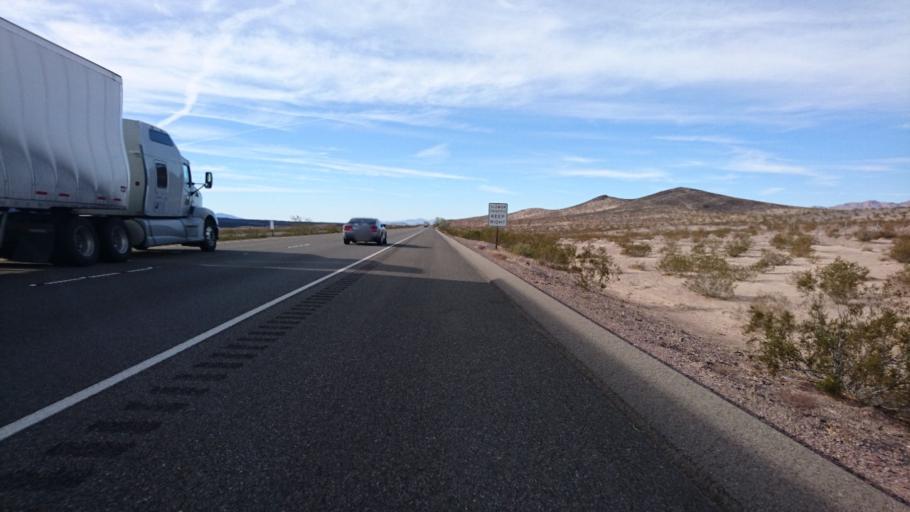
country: US
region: California
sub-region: San Bernardino County
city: Joshua Tree
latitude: 34.7438
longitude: -116.3215
